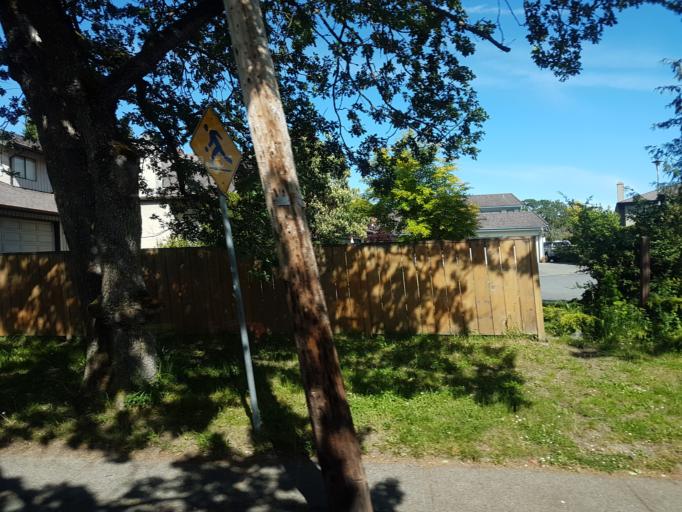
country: CA
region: British Columbia
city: Oak Bay
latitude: 48.4767
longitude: -123.3227
